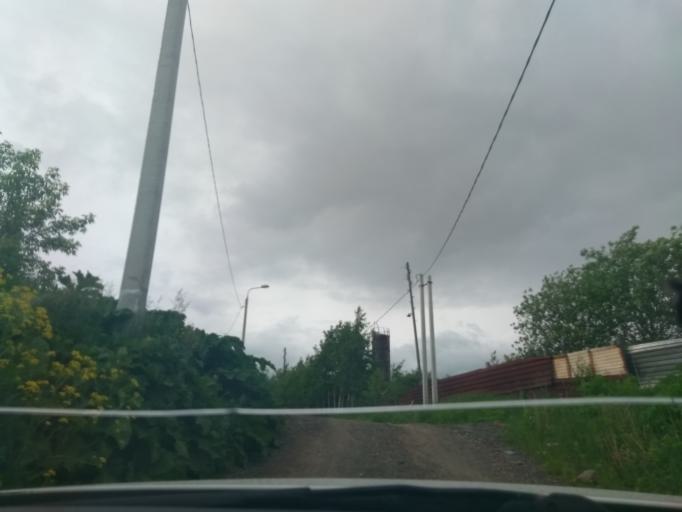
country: RU
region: Perm
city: Perm
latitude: 57.9908
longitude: 56.3384
